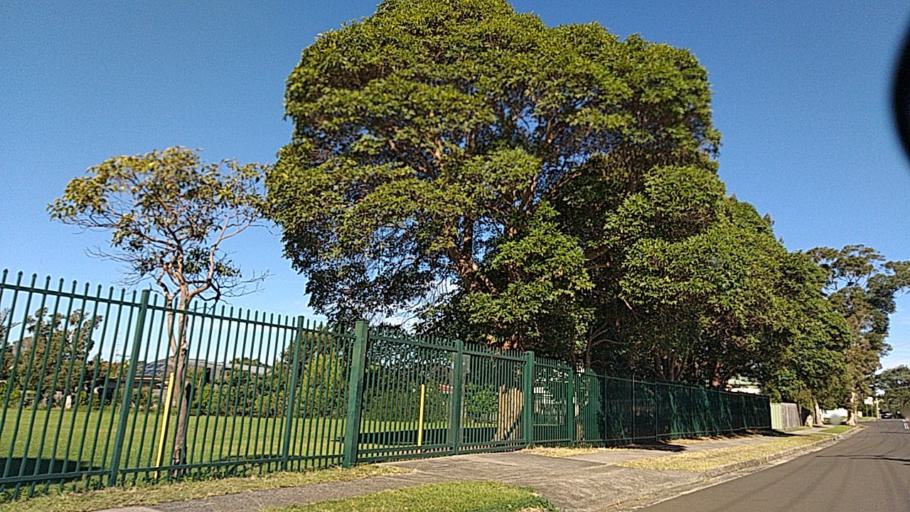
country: AU
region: New South Wales
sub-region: Wollongong
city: Corrimal
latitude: -34.3782
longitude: 150.9049
